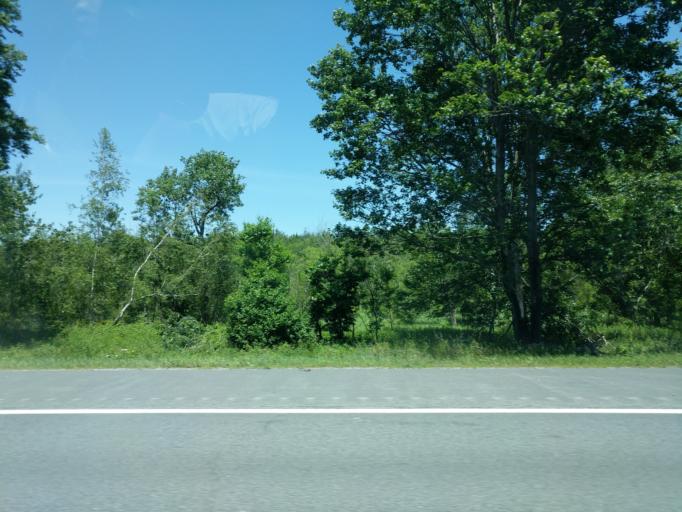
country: US
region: New York
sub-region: Sullivan County
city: Monticello
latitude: 41.6540
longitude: -74.6636
